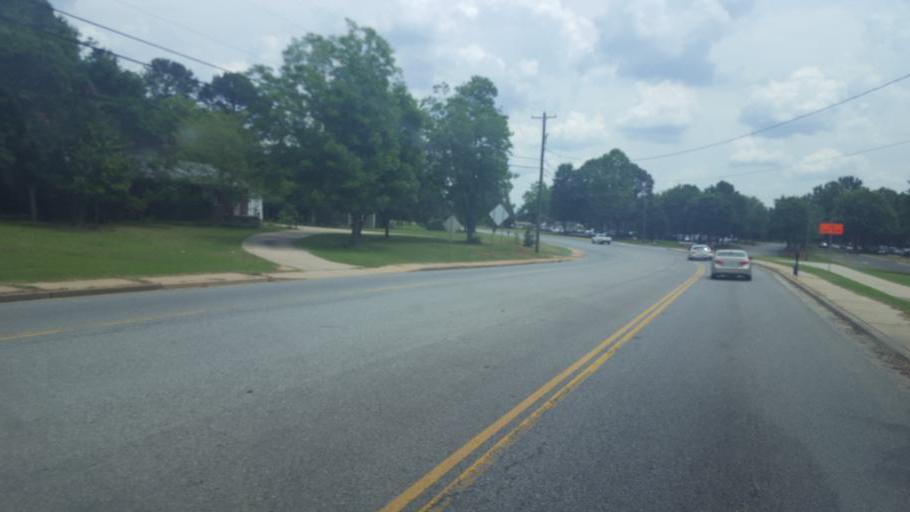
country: US
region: South Carolina
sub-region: York County
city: York
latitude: 34.9852
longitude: -81.2005
